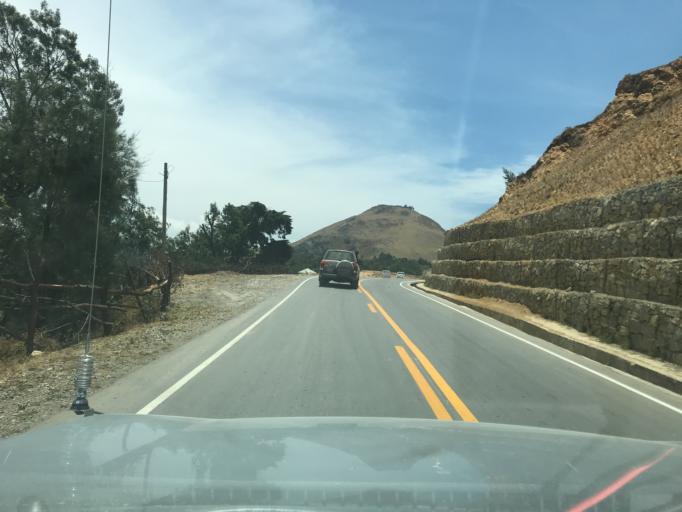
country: TL
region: Manufahi
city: Same
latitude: -8.8776
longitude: 125.5990
